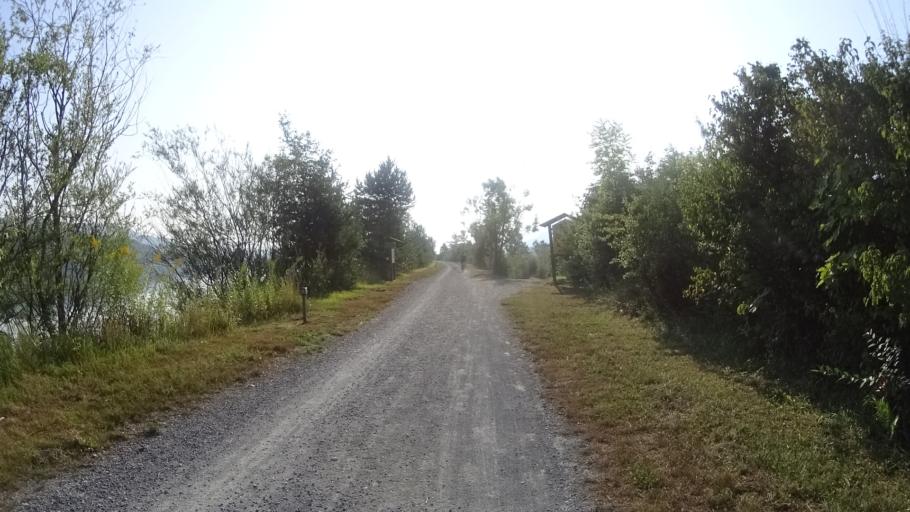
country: AT
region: Carinthia
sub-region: Politischer Bezirk Klagenfurt Land
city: Feistritz im Rosental
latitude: 46.5290
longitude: 14.1541
